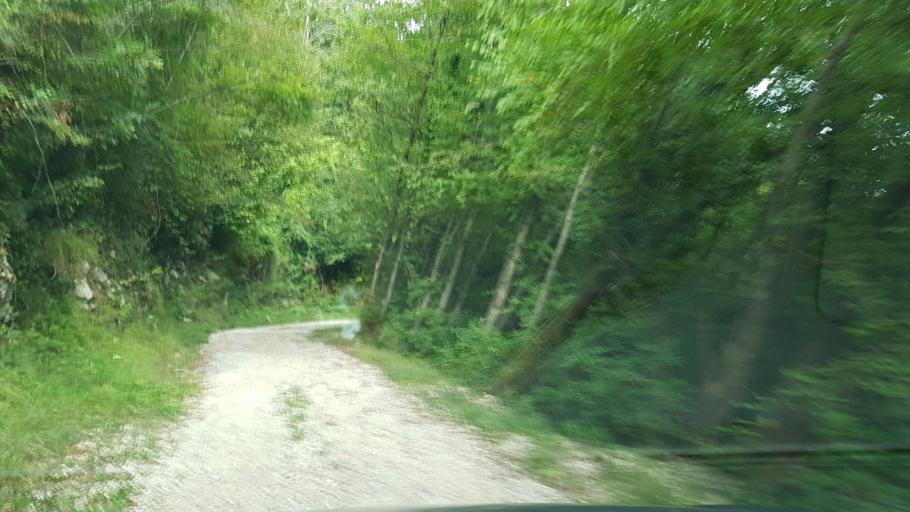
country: SI
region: Kanal
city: Deskle
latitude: 46.0555
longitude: 13.5833
